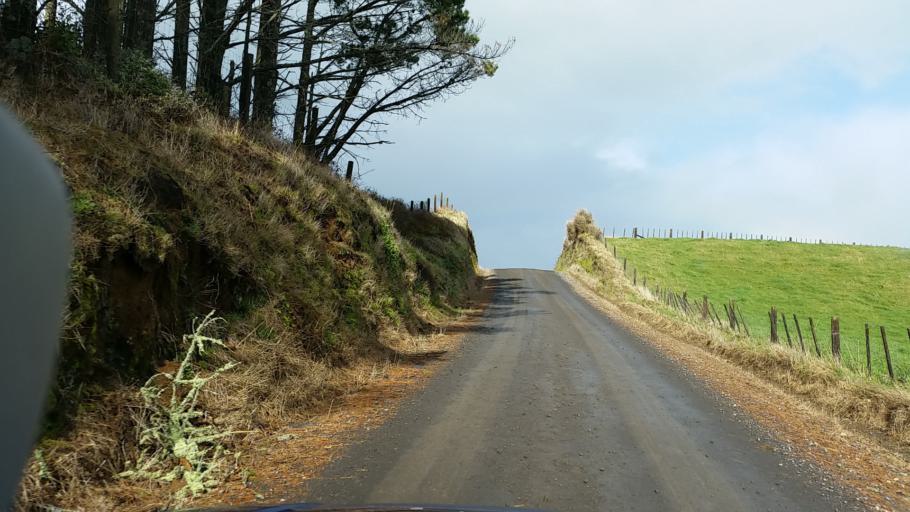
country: NZ
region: Taranaki
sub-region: South Taranaki District
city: Eltham
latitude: -39.2779
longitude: 174.3079
